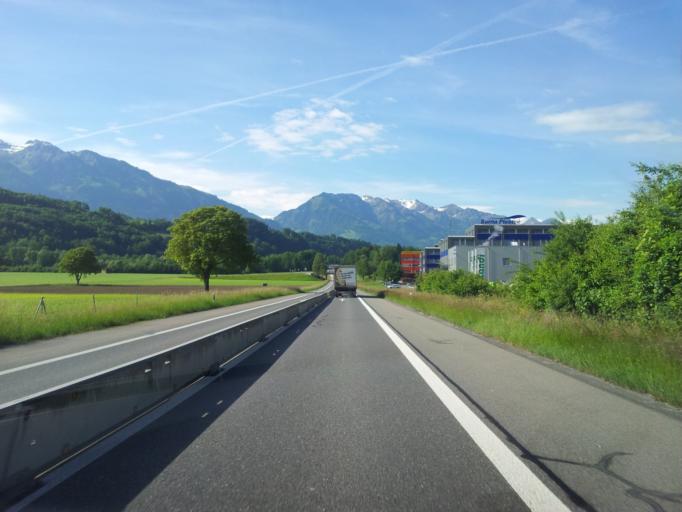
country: CH
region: Obwalden
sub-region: Obwalden
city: Alpnach
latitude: 46.9395
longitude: 8.2777
